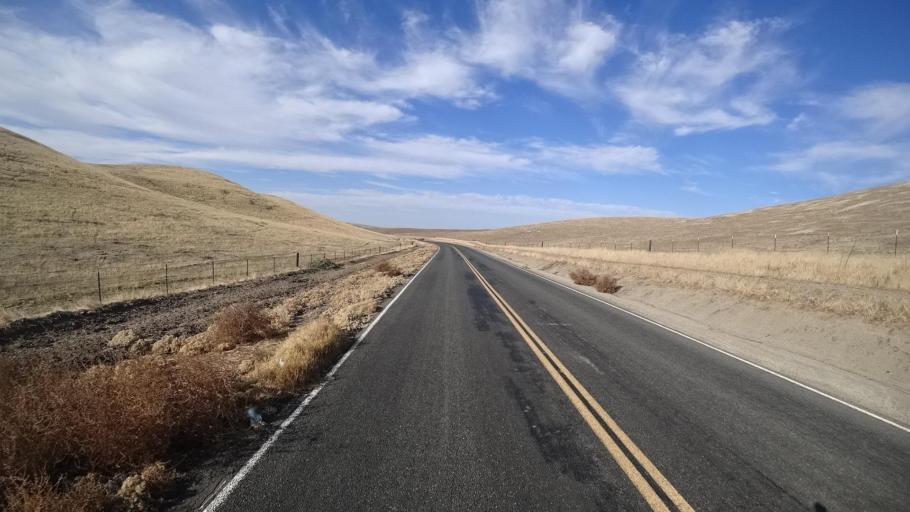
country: US
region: California
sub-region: Kern County
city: Oildale
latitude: 35.6116
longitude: -118.9344
